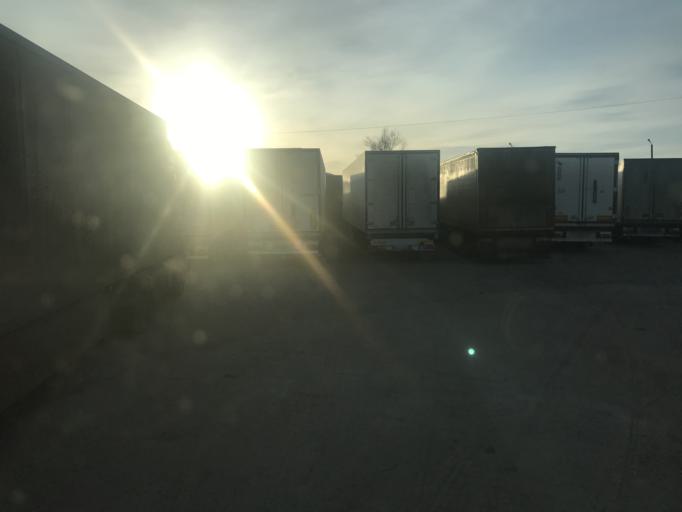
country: AZ
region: Qusar
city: Samur
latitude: 41.6405
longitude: 48.4062
